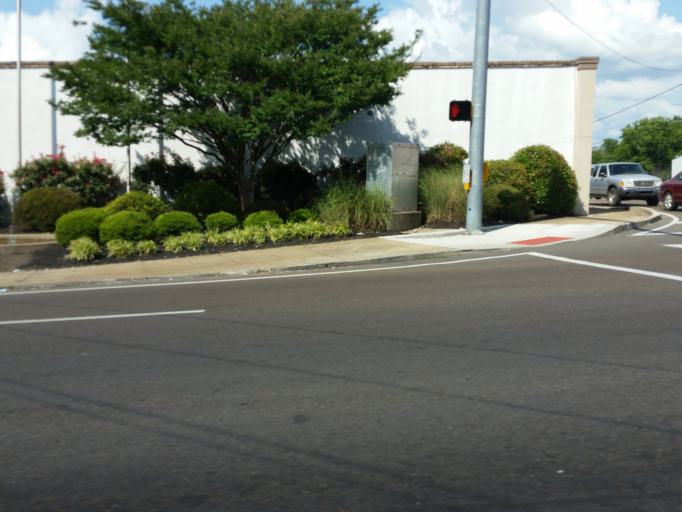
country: US
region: Tennessee
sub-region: Henderson County
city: Lexington
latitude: 35.6510
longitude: -88.3937
